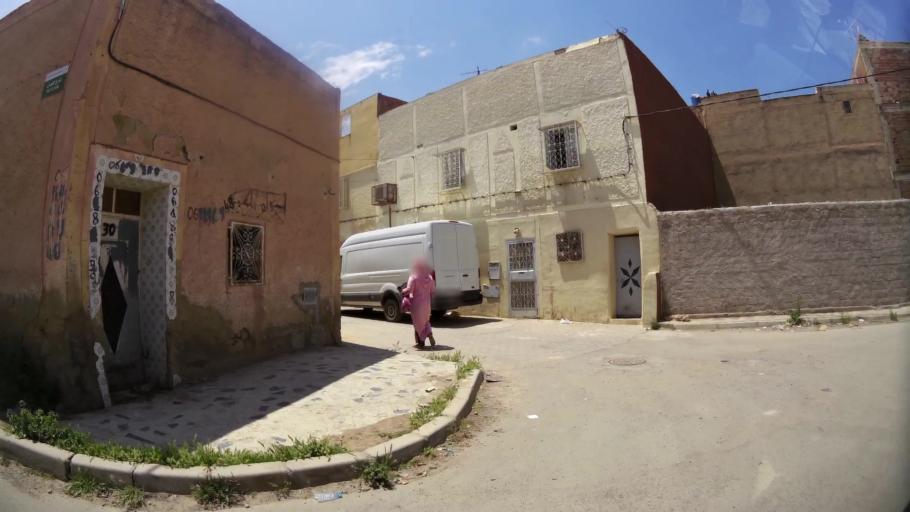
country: MA
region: Oriental
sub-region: Oujda-Angad
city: Oujda
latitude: 34.6834
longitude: -1.8999
